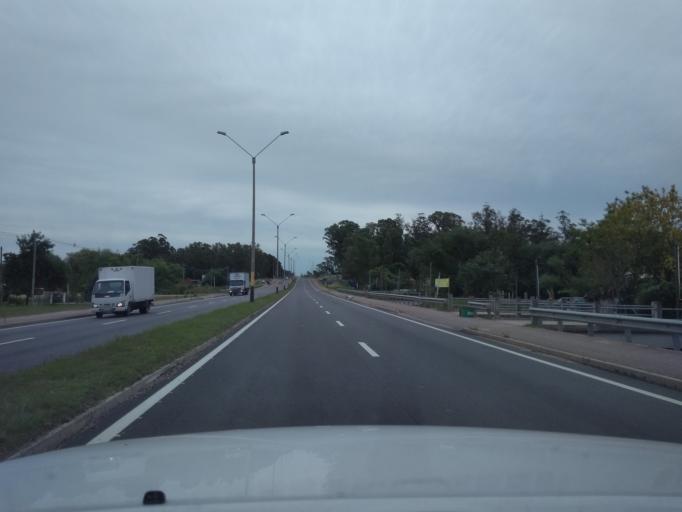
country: UY
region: Canelones
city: Colonia Nicolich
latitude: -34.8102
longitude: -56.0412
